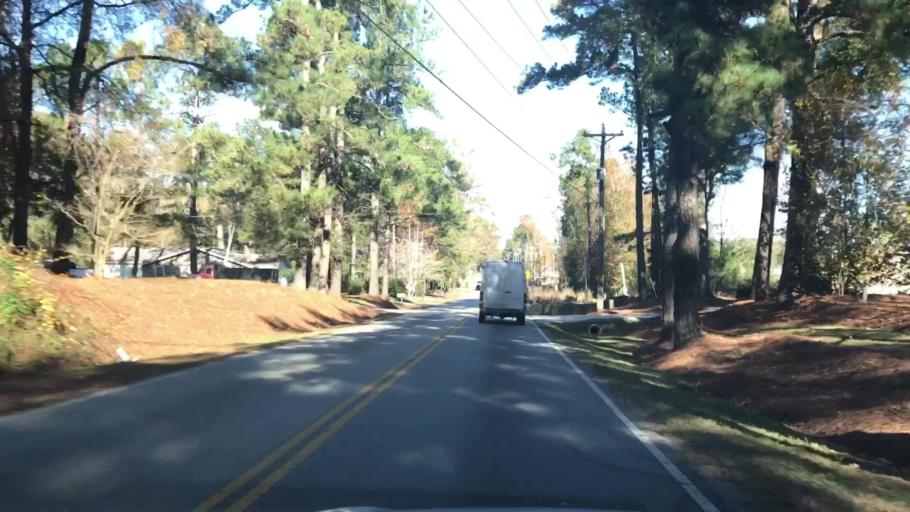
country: US
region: South Carolina
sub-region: Dorchester County
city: Summerville
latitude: 33.0201
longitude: -80.2409
